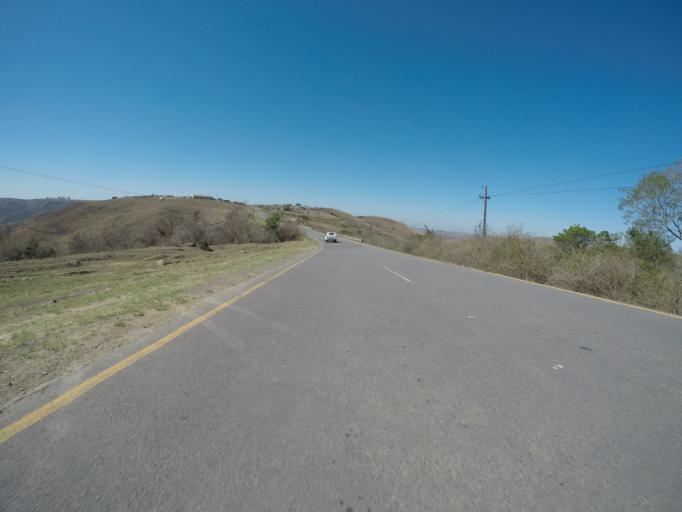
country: ZA
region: Eastern Cape
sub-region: OR Tambo District Municipality
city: Mthatha
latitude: -31.9016
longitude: 28.9461
